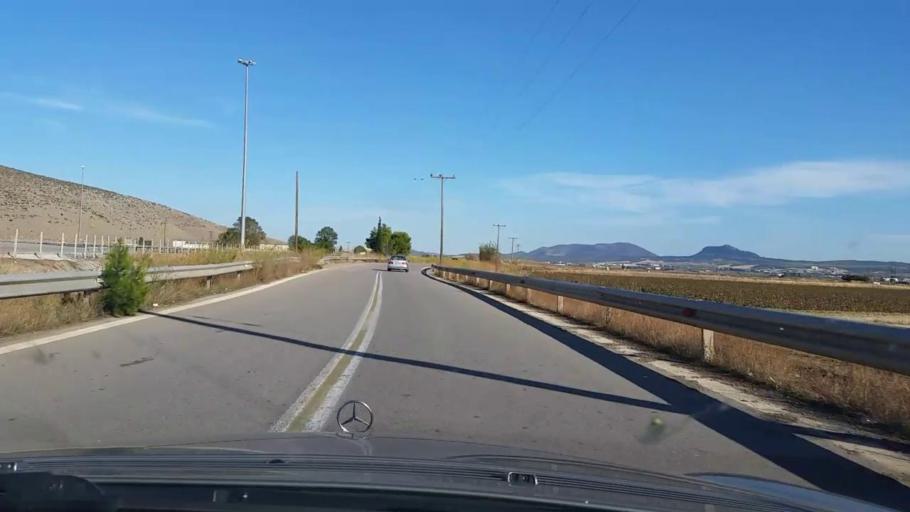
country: GR
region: Central Greece
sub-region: Nomos Voiotias
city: Thivai
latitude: 38.3703
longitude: 23.2867
